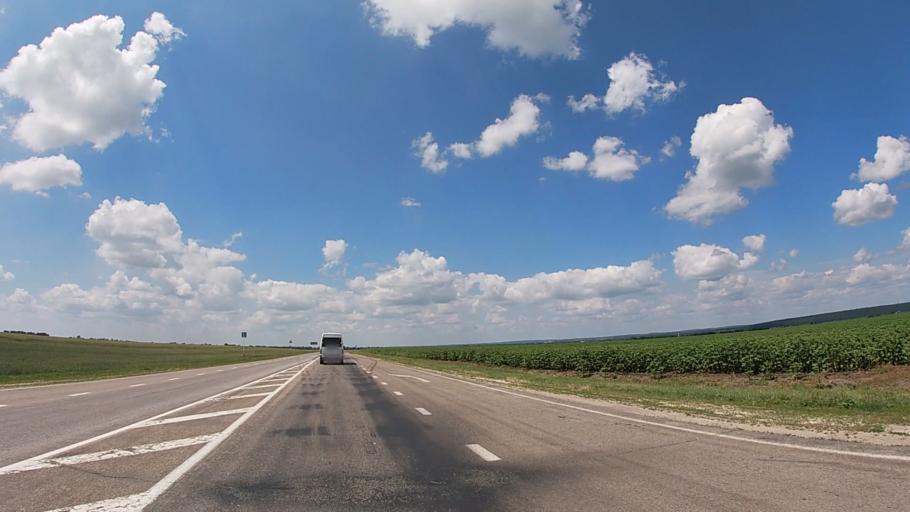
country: RU
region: Belgorod
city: Borisovka
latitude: 50.5771
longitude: 36.0274
